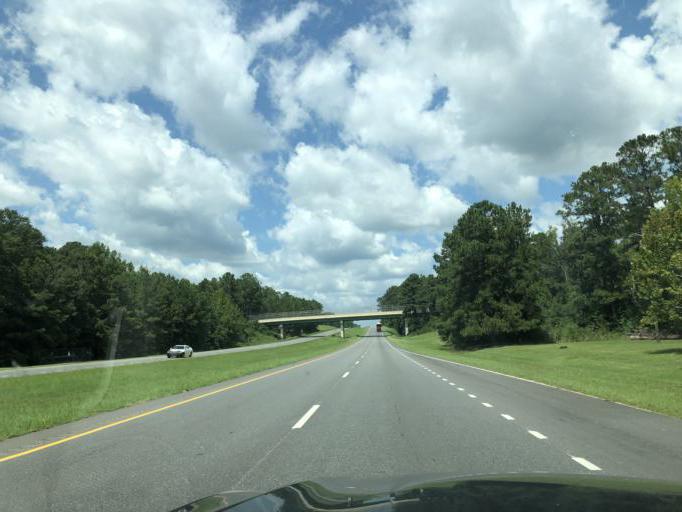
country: US
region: Alabama
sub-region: Barbour County
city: Eufaula
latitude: 31.9884
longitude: -85.1145
